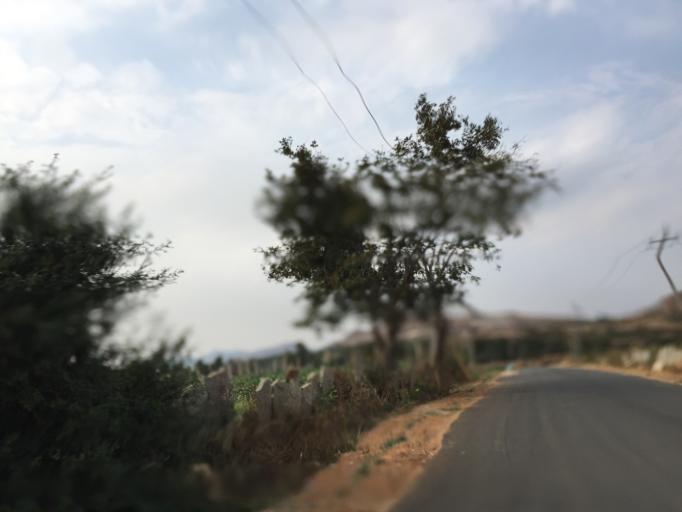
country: IN
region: Karnataka
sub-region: Chikkaballapur
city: Gudibanda
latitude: 13.5700
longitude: 77.7296
